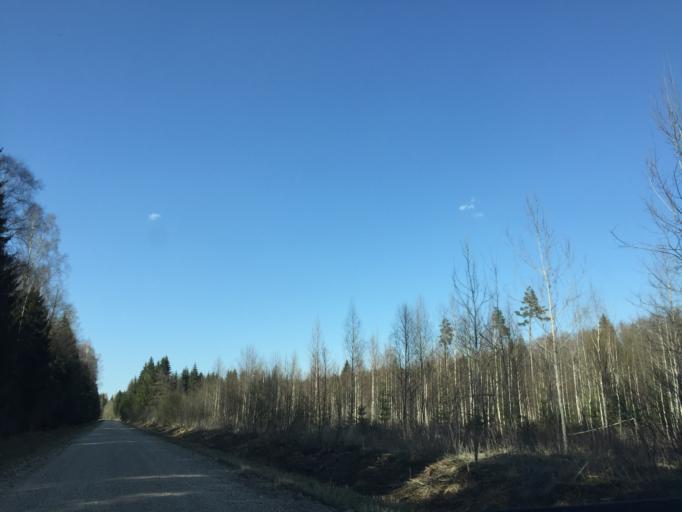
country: LV
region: Kegums
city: Kegums
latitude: 56.8753
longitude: 24.8002
